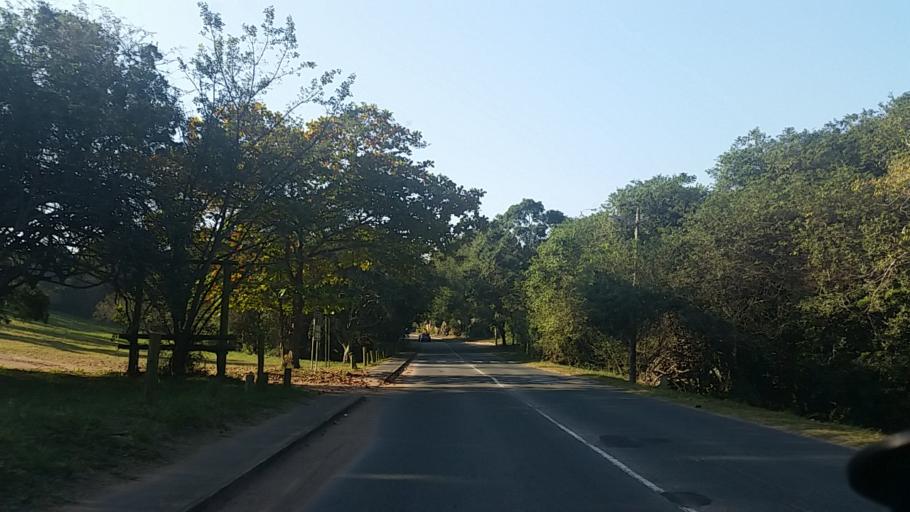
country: ZA
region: KwaZulu-Natal
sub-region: eThekwini Metropolitan Municipality
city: Berea
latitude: -29.8397
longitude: 30.9232
